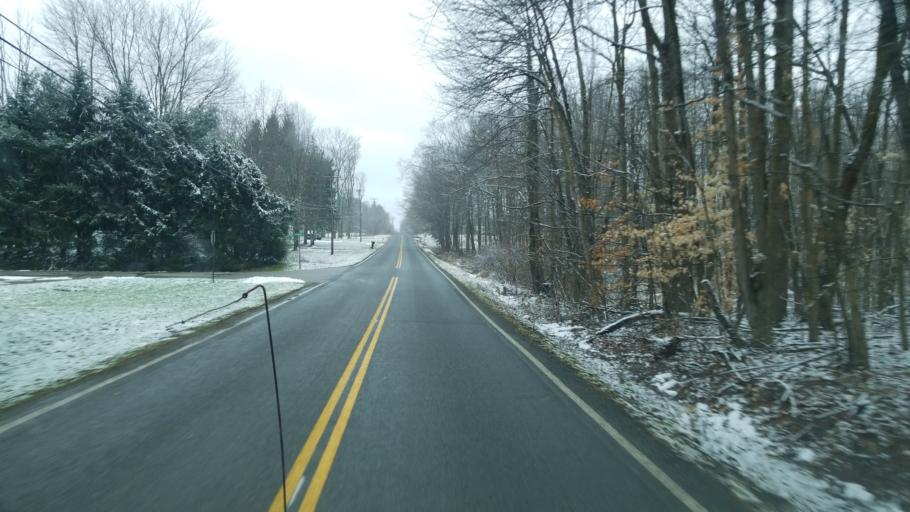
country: US
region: Ohio
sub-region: Portage County
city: Mantua
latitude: 41.3010
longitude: -81.2455
